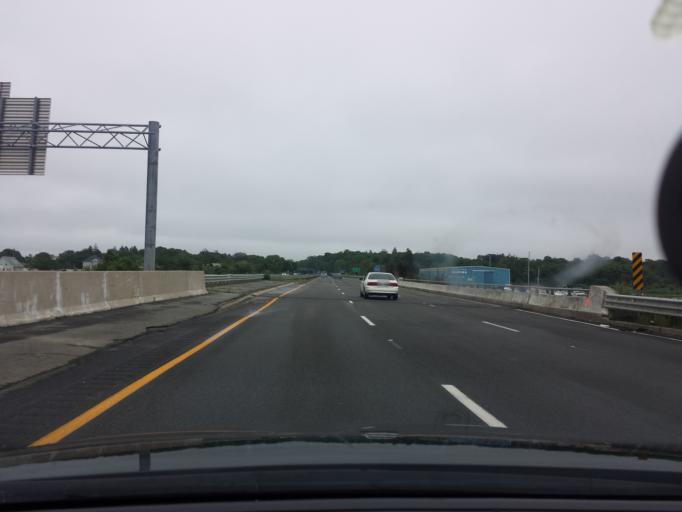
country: US
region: Massachusetts
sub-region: Bristol County
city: Fairhaven
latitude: 41.6548
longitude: -70.9183
